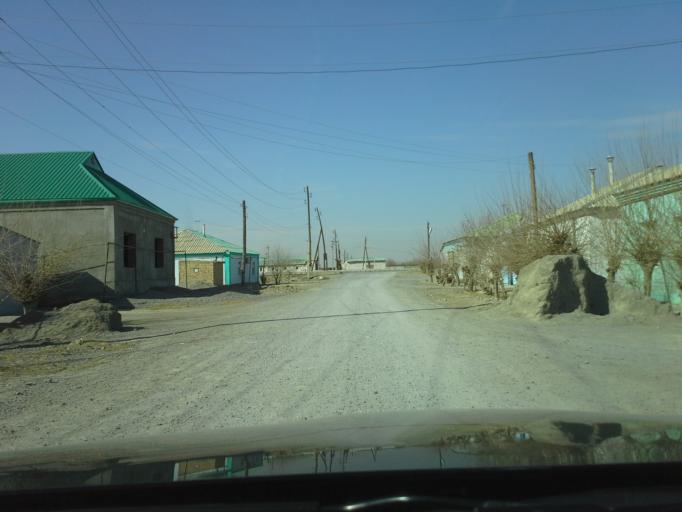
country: TM
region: Ahal
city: Abadan
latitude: 38.1052
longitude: 58.0302
